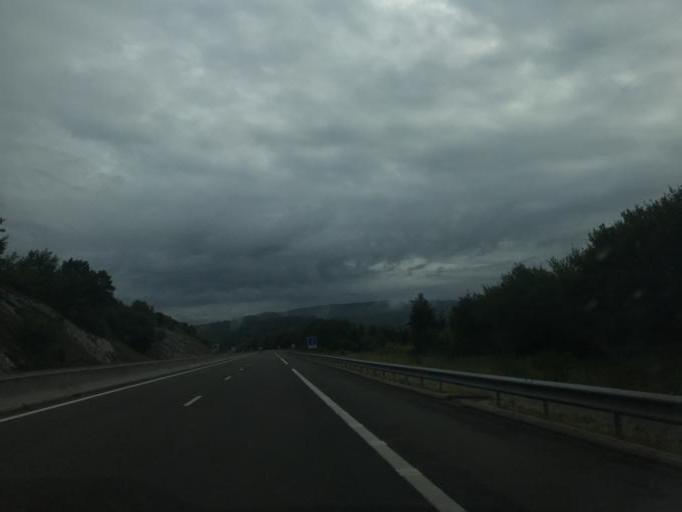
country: FR
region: Rhone-Alpes
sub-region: Departement de l'Ain
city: Oyonnax
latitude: 46.2778
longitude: 5.6575
